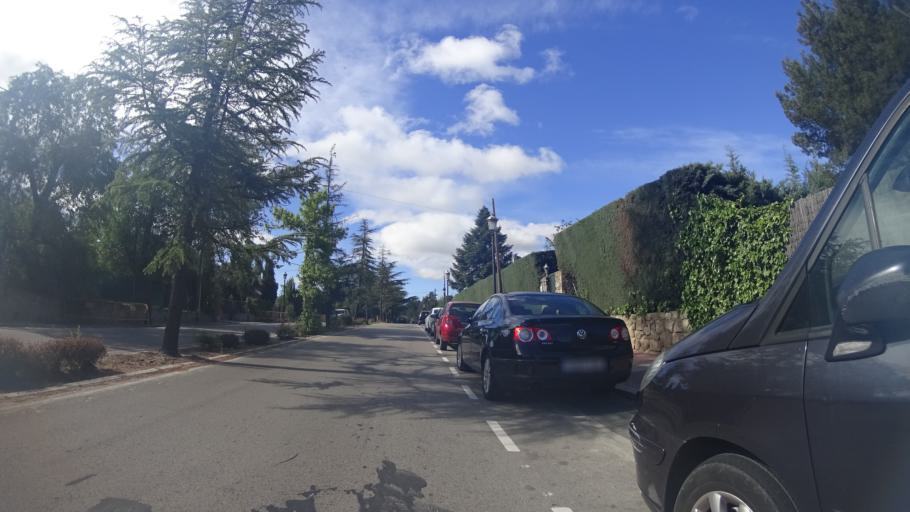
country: ES
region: Madrid
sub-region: Provincia de Madrid
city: Villanueva del Pardillo
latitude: 40.4826
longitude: -3.9381
